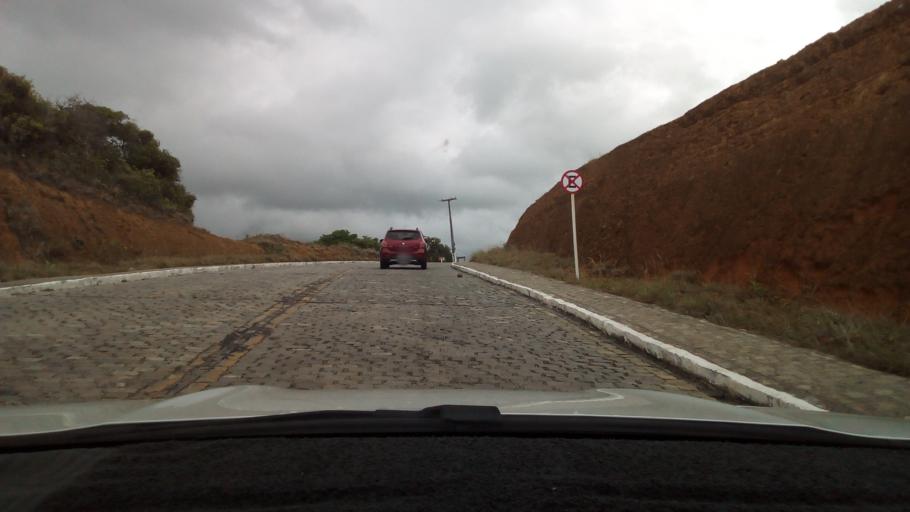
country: BR
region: Paraiba
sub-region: Pitimbu
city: Pitimbu
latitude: -7.3640
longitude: -34.7999
